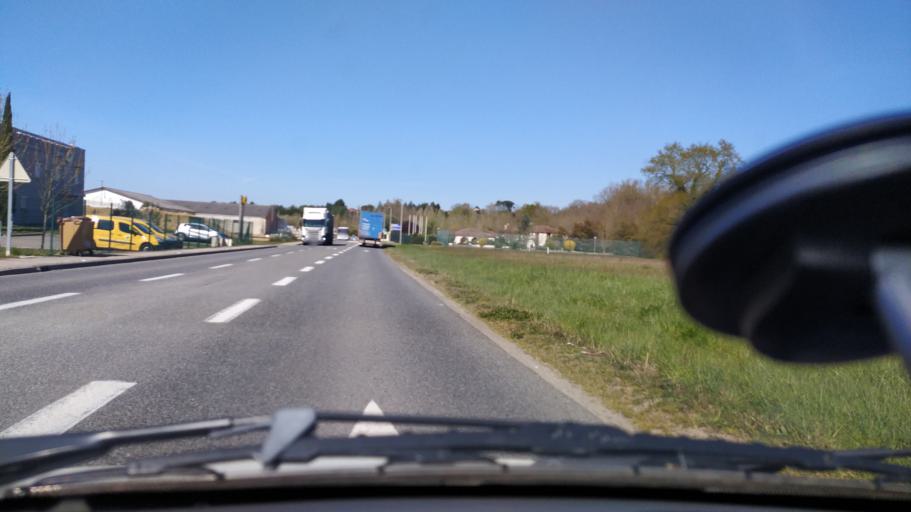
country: FR
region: Midi-Pyrenees
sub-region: Departement du Gers
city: Nogaro
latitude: 43.7678
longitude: -0.0312
